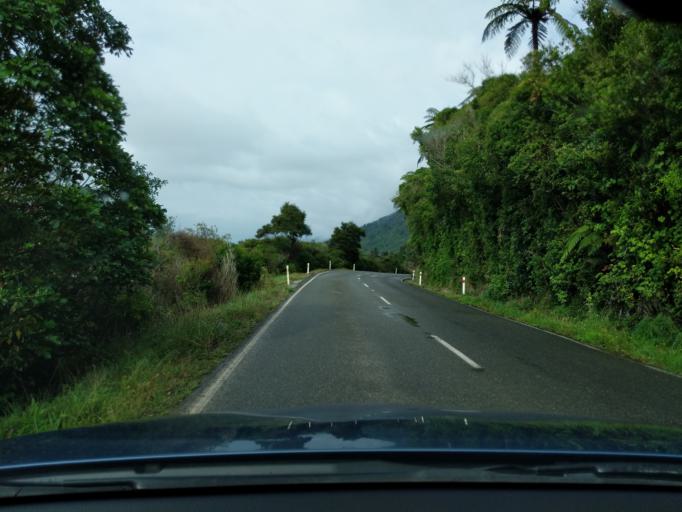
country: NZ
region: Tasman
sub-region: Tasman District
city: Takaka
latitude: -40.6537
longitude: 172.6516
